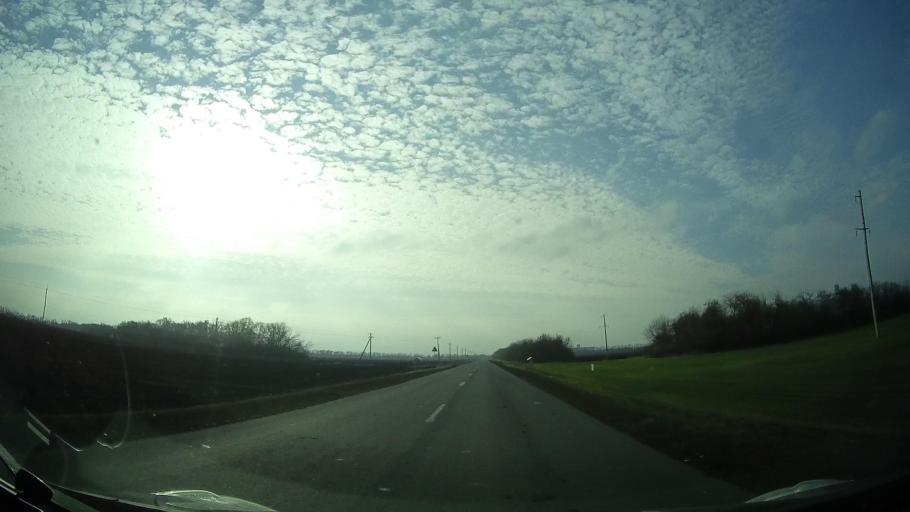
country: RU
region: Rostov
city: Mechetinskaya
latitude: 46.7990
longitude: 40.5114
